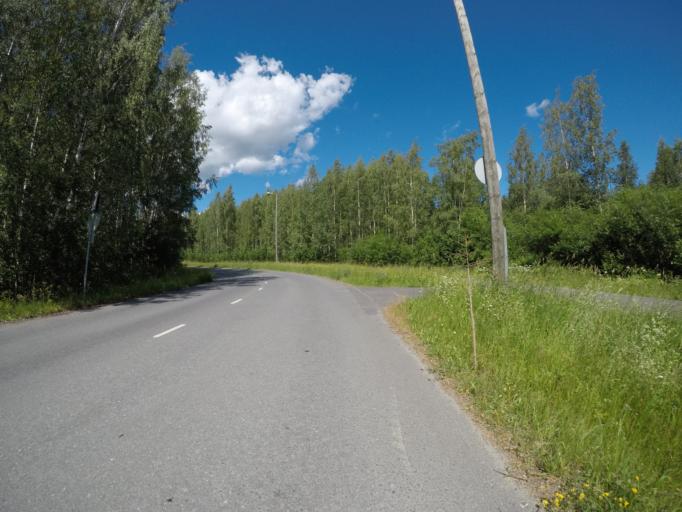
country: FI
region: Haeme
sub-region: Haemeenlinna
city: Haemeenlinna
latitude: 61.0220
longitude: 24.4263
